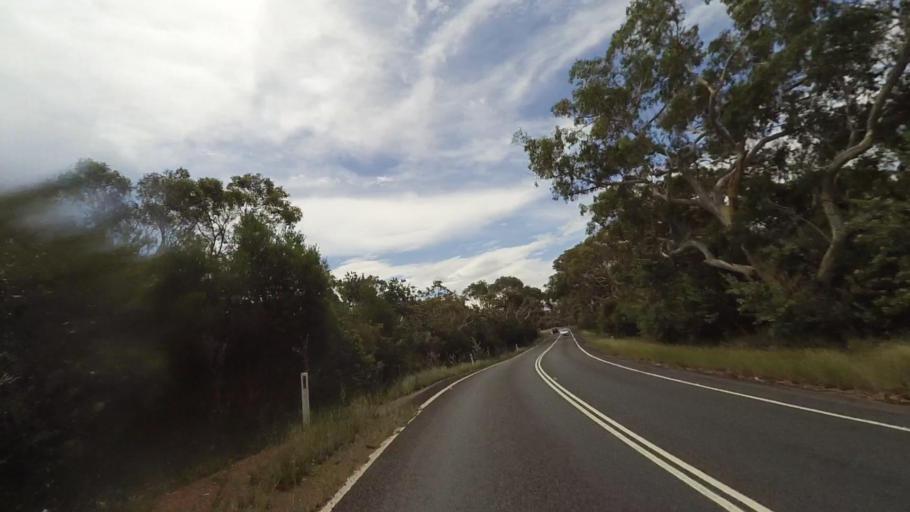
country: AU
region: New South Wales
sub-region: Sutherland Shire
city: Grays Point
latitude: -34.0843
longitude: 151.0638
